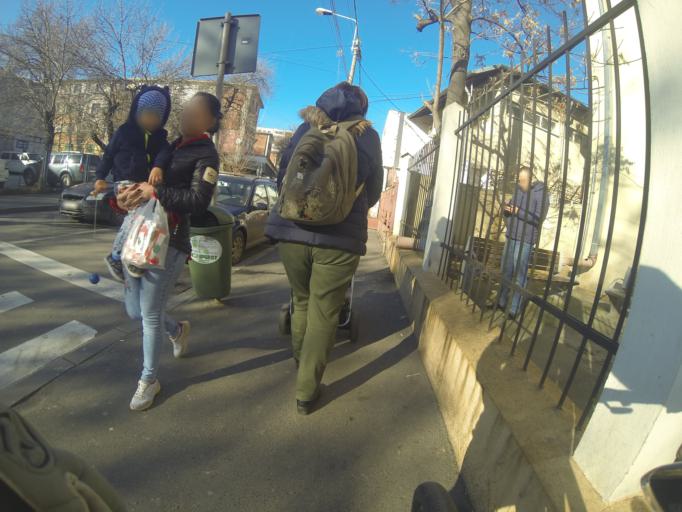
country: RO
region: Bucuresti
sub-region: Municipiul Bucuresti
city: Bucuresti
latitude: 44.4050
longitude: 26.0648
